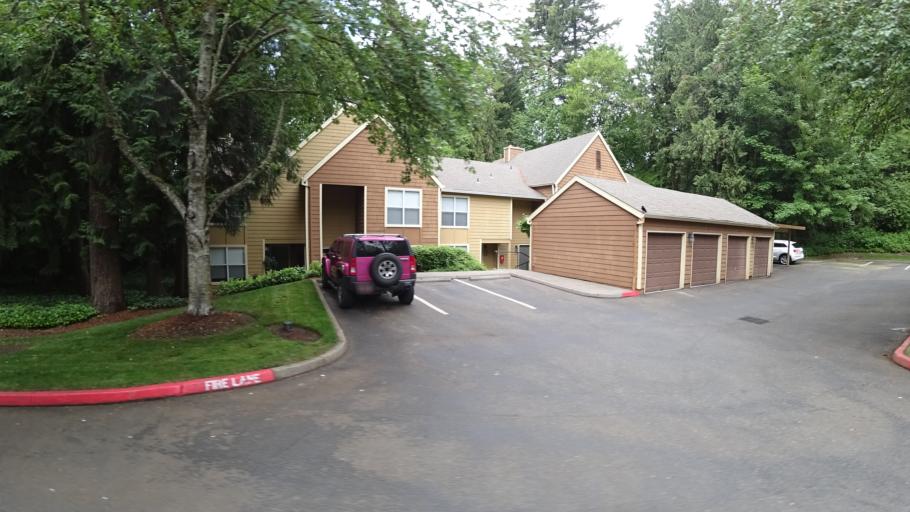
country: US
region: Oregon
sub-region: Washington County
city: Garden Home-Whitford
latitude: 45.4689
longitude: -122.7532
